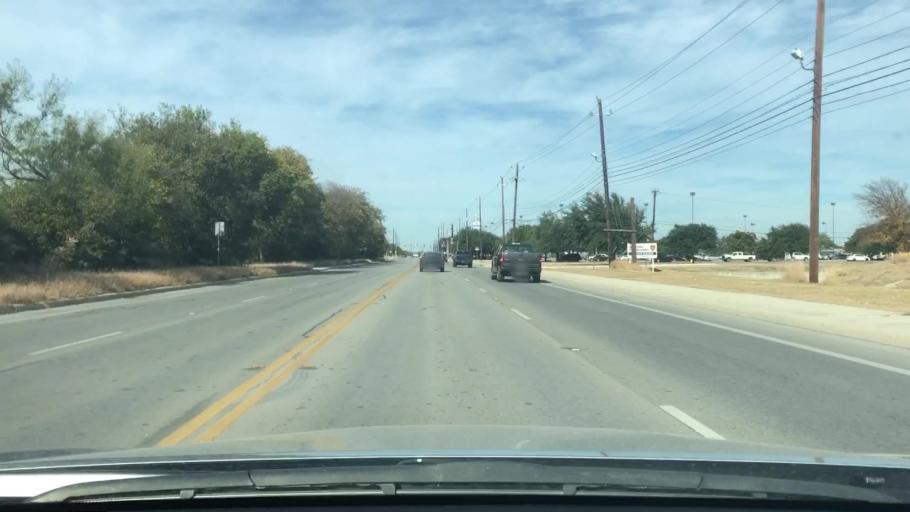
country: US
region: Texas
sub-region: Bexar County
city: Lackland Air Force Base
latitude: 29.4312
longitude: -98.5997
